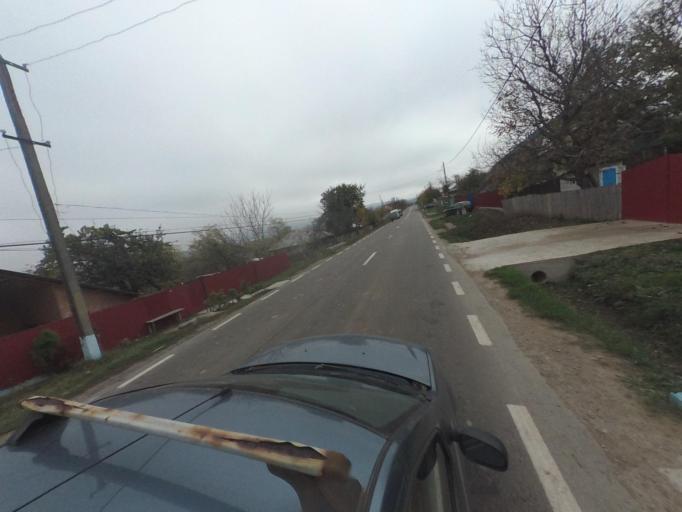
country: RO
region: Vaslui
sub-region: Comuna Bacesti
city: Bacesti
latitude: 46.8327
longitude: 27.2336
